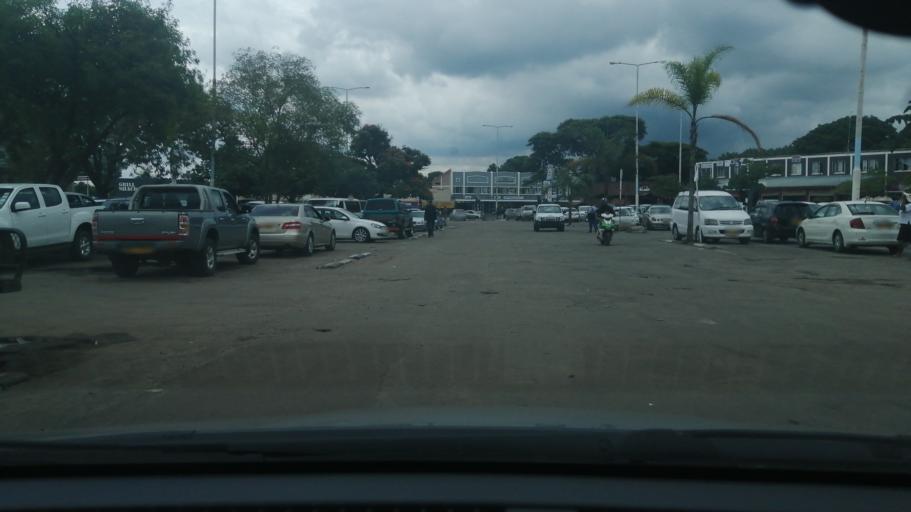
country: ZW
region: Harare
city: Harare
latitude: -17.8030
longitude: 31.0384
